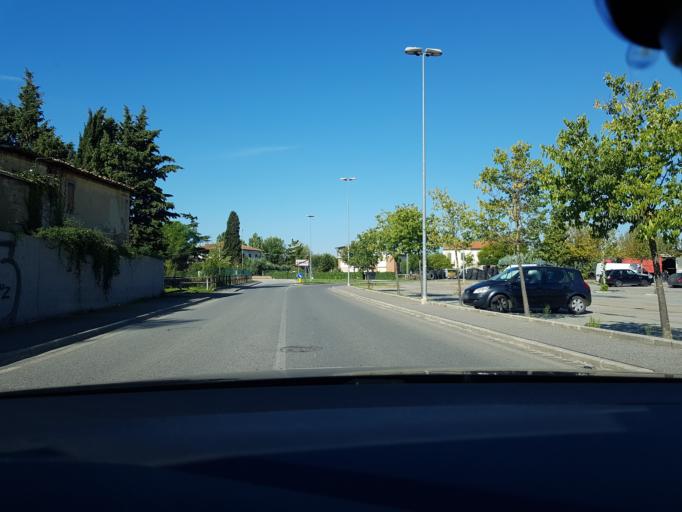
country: IT
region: Tuscany
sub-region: Province of Florence
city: Empoli
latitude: 43.7127
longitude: 10.9203
